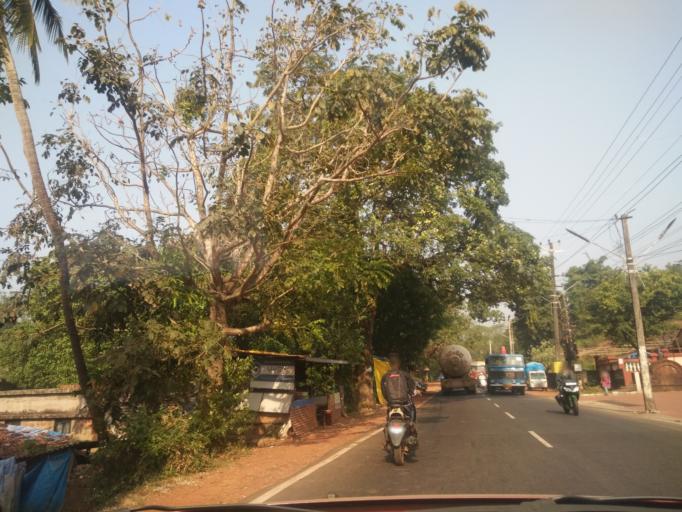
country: IN
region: Goa
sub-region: North Goa
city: Queula
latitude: 15.3599
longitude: 74.0006
